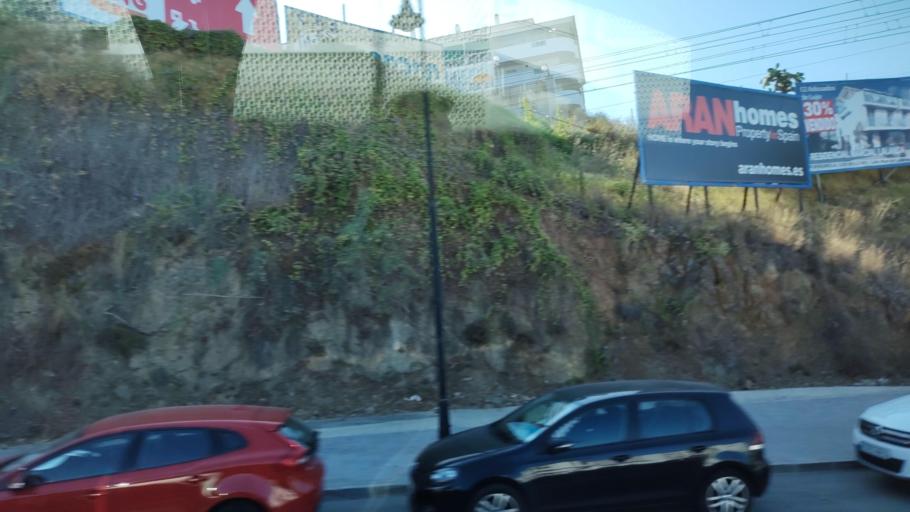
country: ES
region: Andalusia
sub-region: Provincia de Malaga
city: Benalmadena
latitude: 36.5676
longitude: -4.5967
